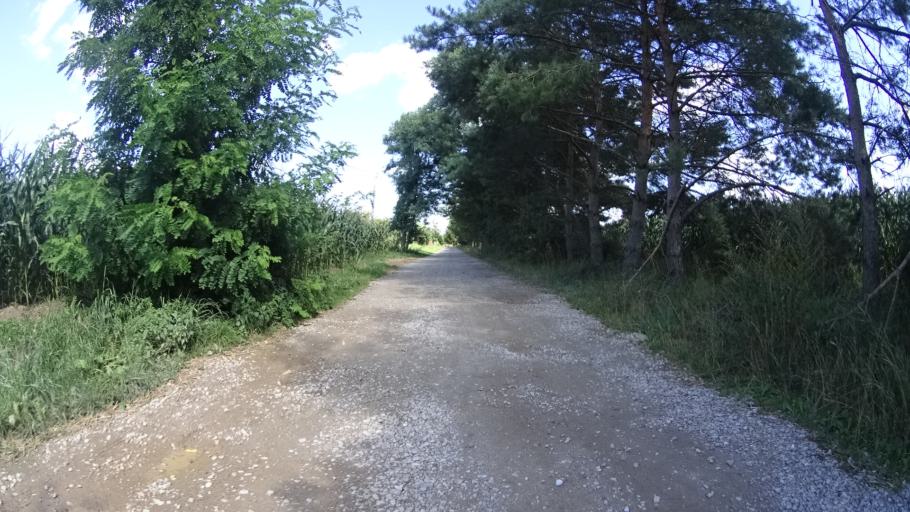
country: PL
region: Masovian Voivodeship
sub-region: Powiat grojecki
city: Mogielnica
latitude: 51.6803
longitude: 20.7610
